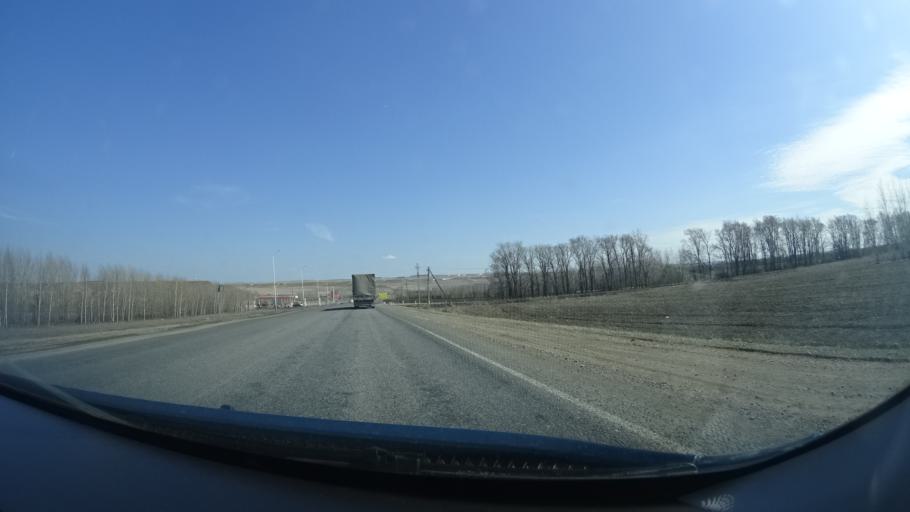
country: RU
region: Bashkortostan
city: Subkhankulovo
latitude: 54.4852
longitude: 53.8962
